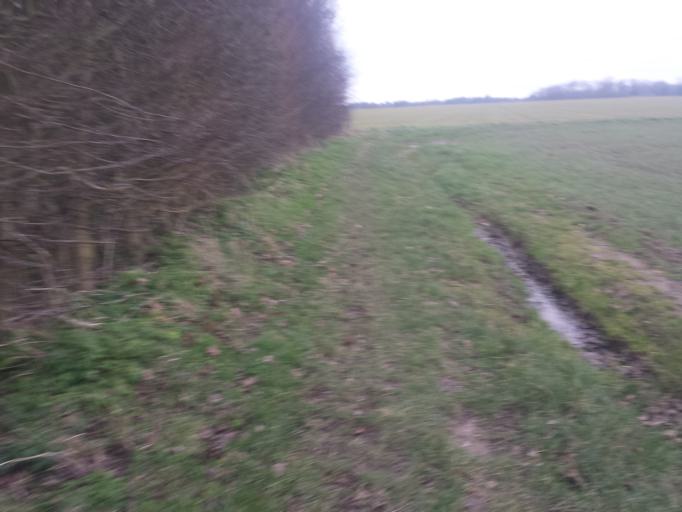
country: GB
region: England
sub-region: Essex
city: Little Clacton
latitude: 51.8781
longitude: 1.1632
